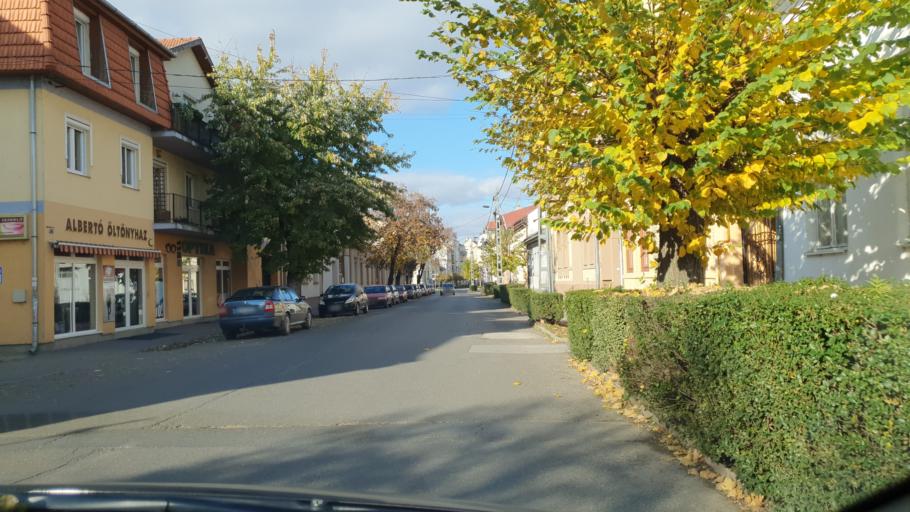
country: HU
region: Szabolcs-Szatmar-Bereg
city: Kisvarda
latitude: 48.2224
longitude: 22.0793
